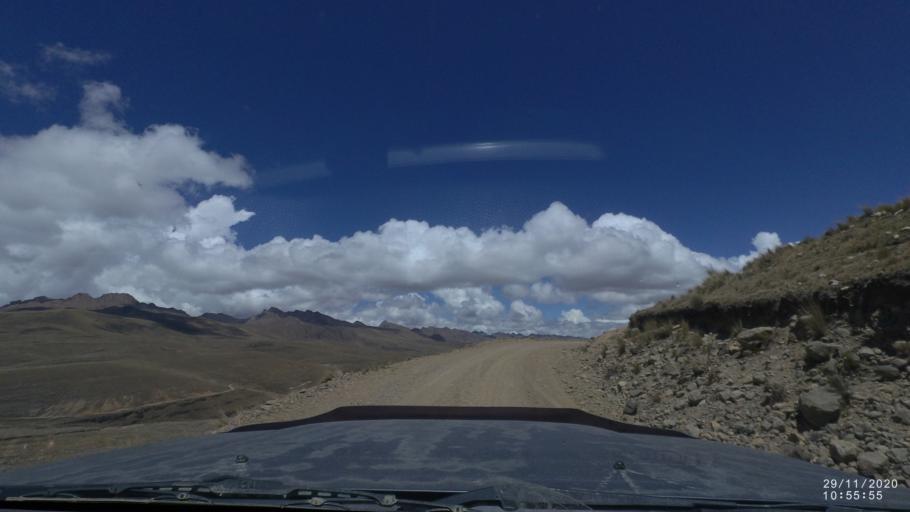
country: BO
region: Cochabamba
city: Cochabamba
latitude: -17.2227
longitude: -66.2235
